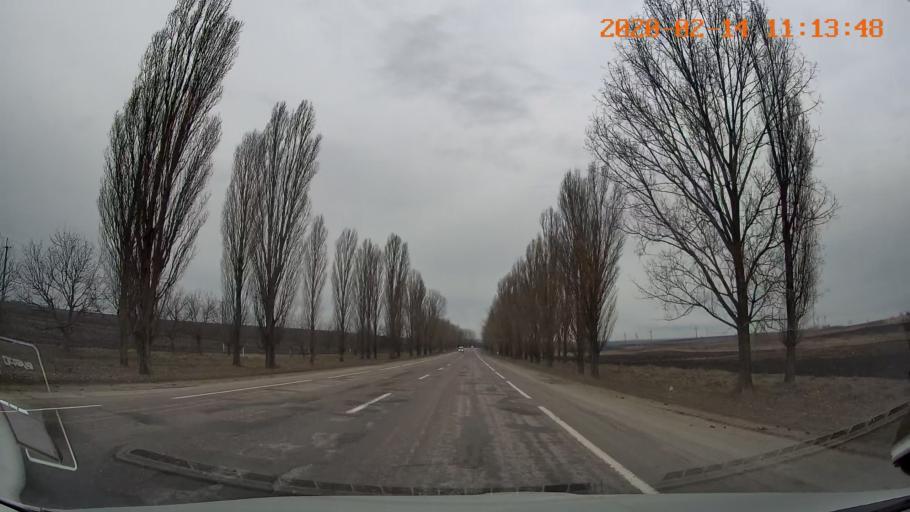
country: MD
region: Raionul Edinet
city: Edinet
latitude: 48.2175
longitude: 27.2334
